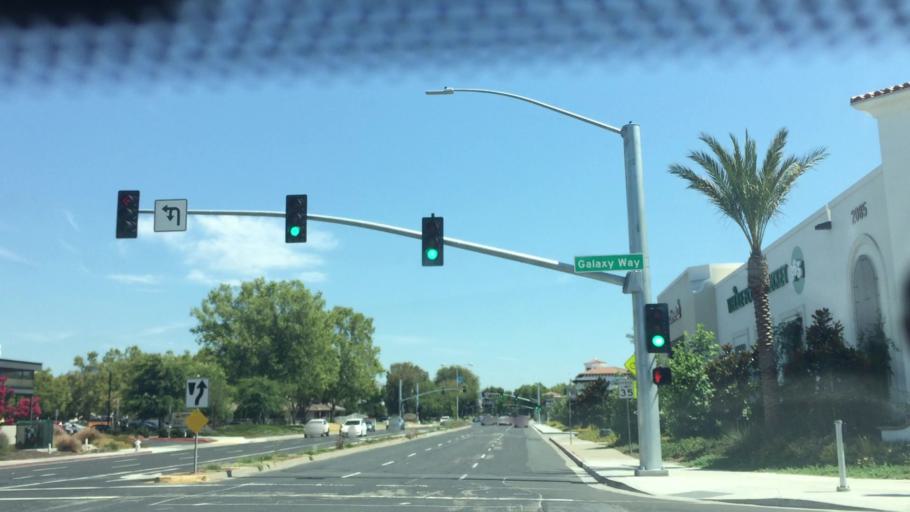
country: US
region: California
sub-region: Contra Costa County
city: Pacheco
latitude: 37.9747
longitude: -122.0587
